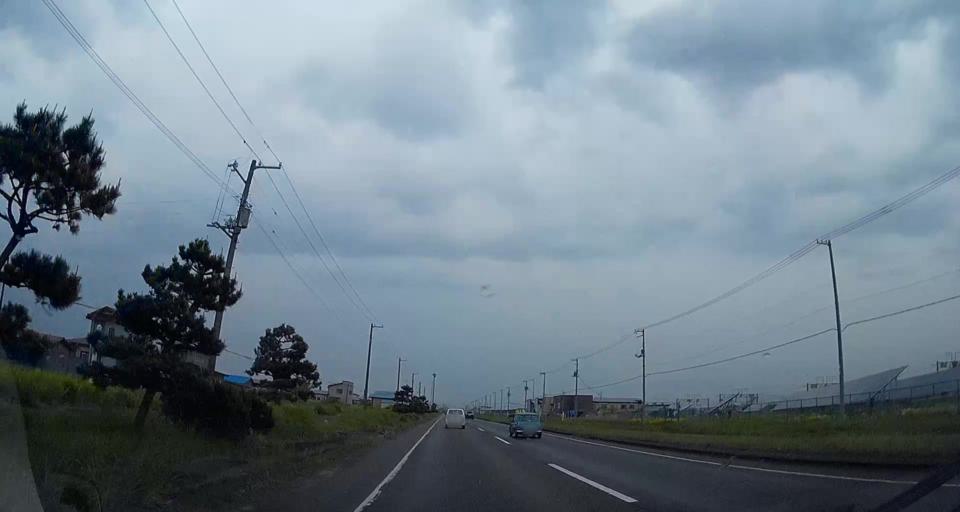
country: JP
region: Hokkaido
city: Tomakomai
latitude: 42.6032
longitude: 141.4920
